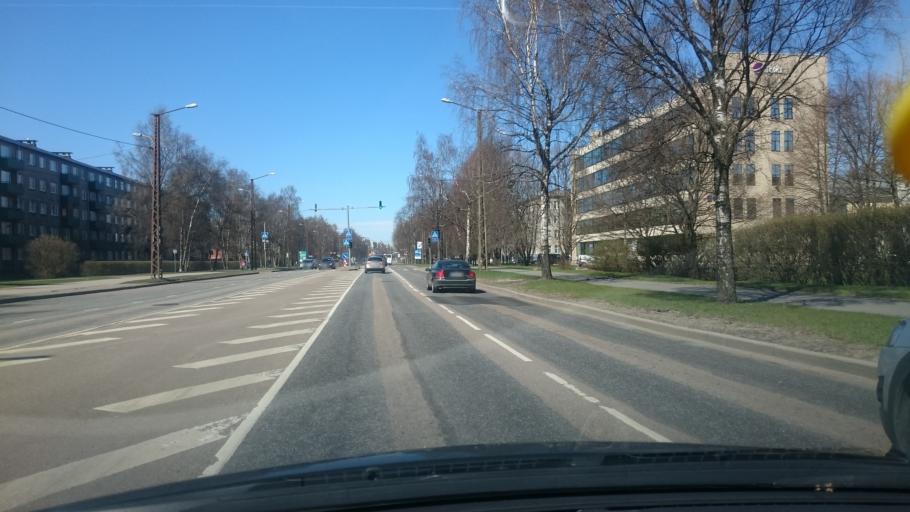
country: EE
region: Harju
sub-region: Tallinna linn
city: Tallinn
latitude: 59.4339
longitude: 24.7143
